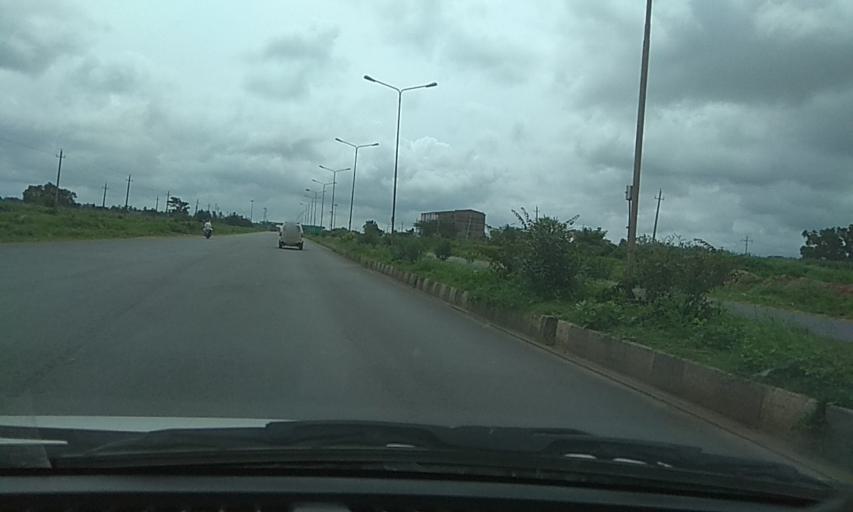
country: IN
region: Karnataka
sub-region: Davanagere
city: Mayakonda
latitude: 14.3772
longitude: 76.1012
